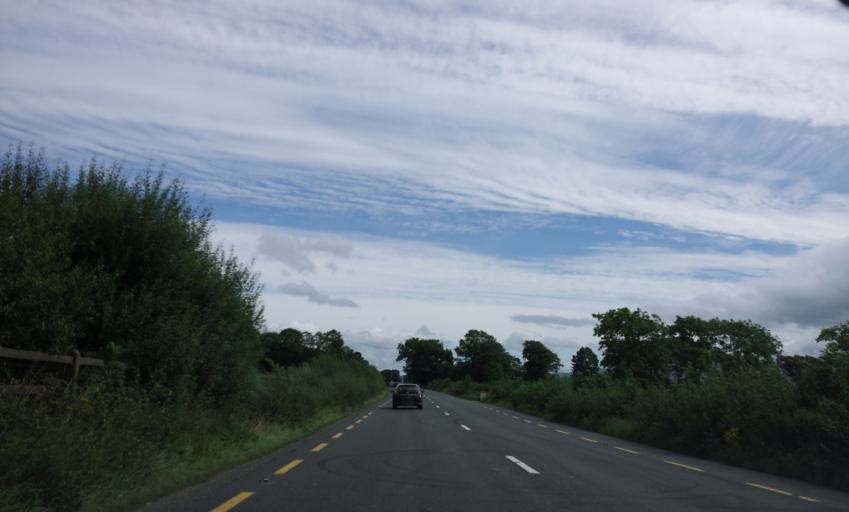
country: IE
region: Munster
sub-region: Ciarrai
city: Cill Airne
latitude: 52.0737
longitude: -9.6167
